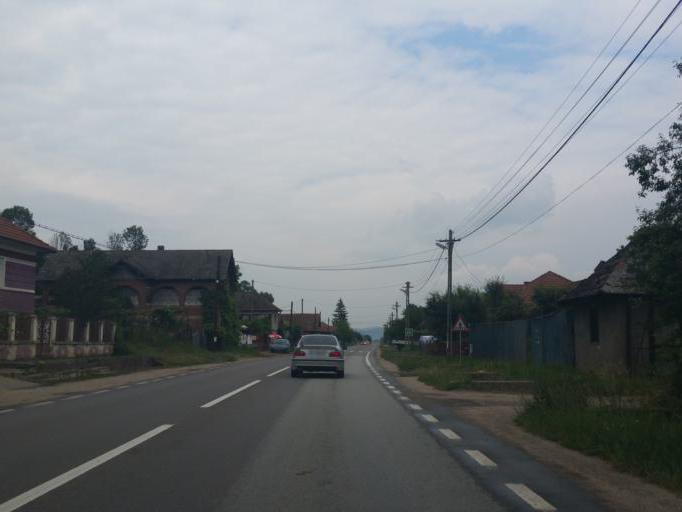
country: RO
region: Salaj
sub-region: Comuna Zimbor
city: Zimbor
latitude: 47.0029
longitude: 23.2565
